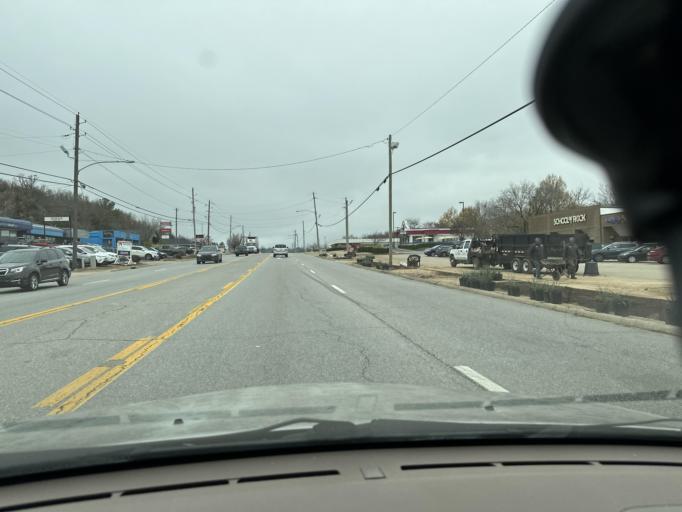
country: US
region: Arkansas
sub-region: Washington County
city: Johnson
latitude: 36.1034
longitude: -94.1481
